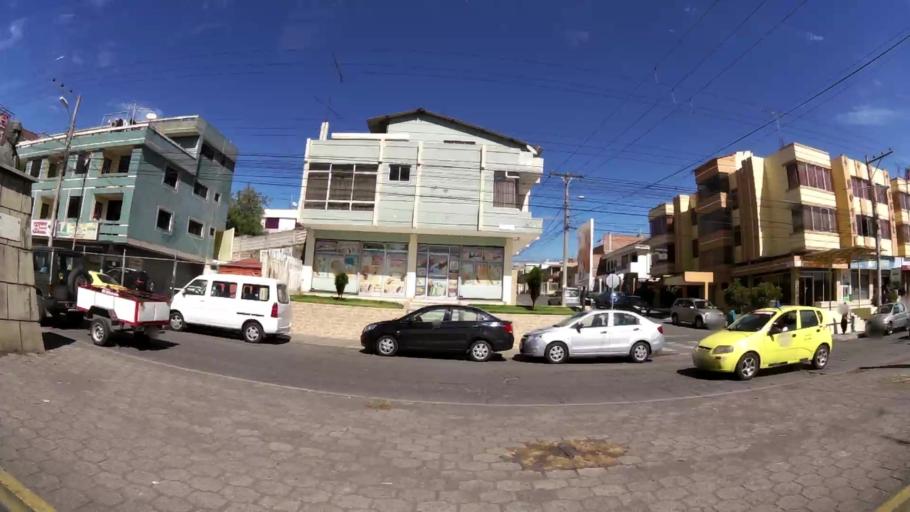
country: EC
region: Chimborazo
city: Riobamba
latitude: -1.6634
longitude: -78.6640
